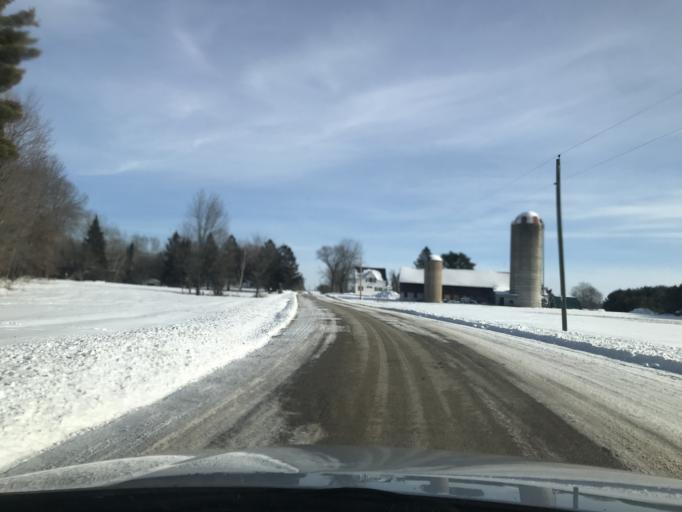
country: US
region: Wisconsin
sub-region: Oconto County
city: Gillett
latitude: 45.1202
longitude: -88.2493
